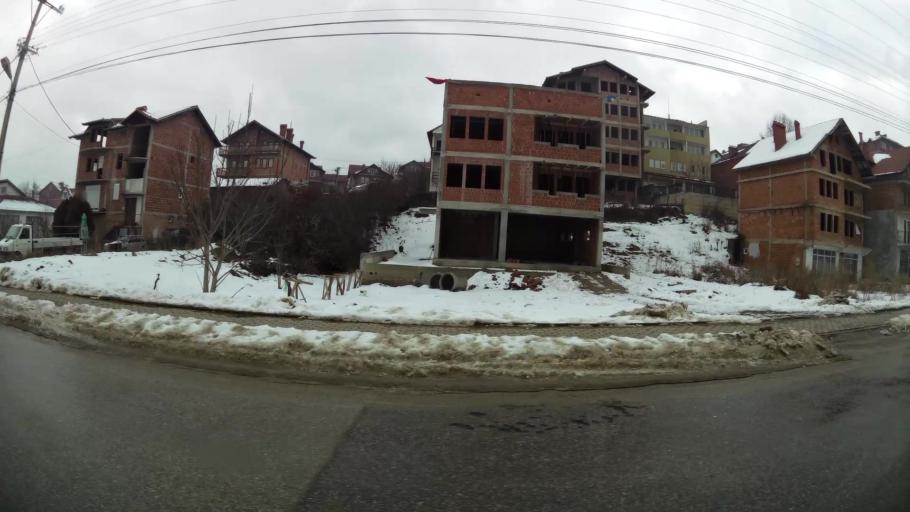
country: XK
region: Pristina
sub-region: Komuna e Prishtines
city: Pristina
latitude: 42.6784
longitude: 21.1791
